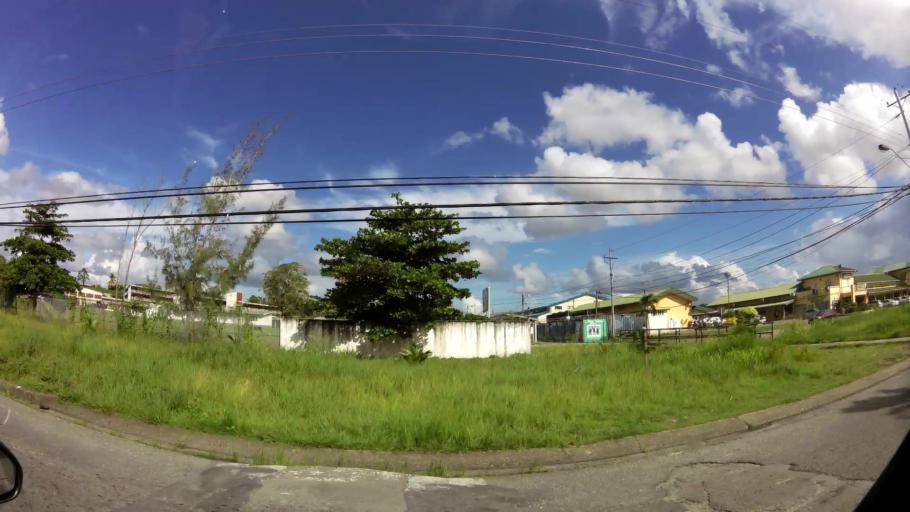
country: TT
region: City of San Fernando
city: Mon Repos
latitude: 10.2683
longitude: -61.4486
